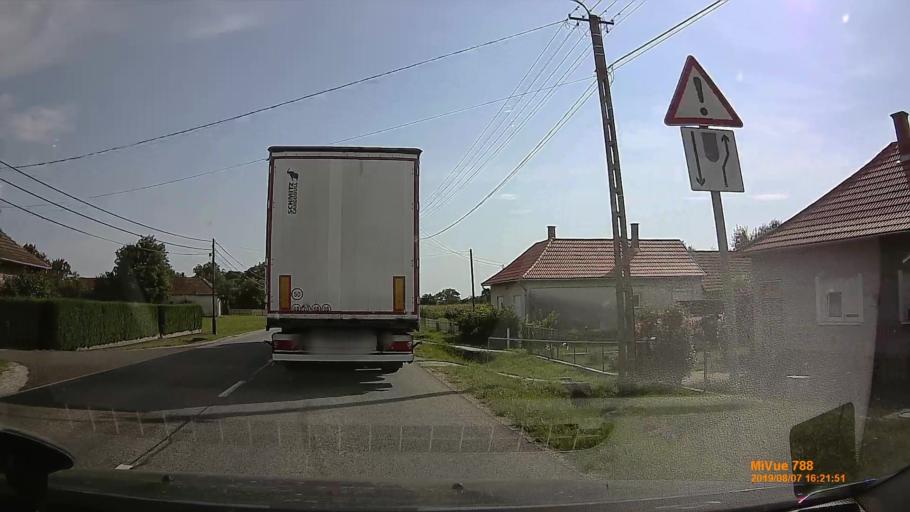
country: HU
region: Zala
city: Zalalovo
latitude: 46.7601
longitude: 16.5631
